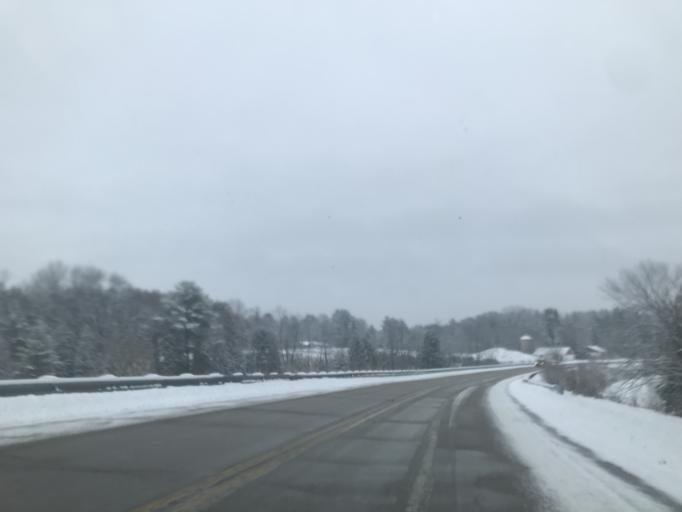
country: US
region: Wisconsin
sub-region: Oconto County
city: Oconto Falls
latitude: 44.8630
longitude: -88.0607
